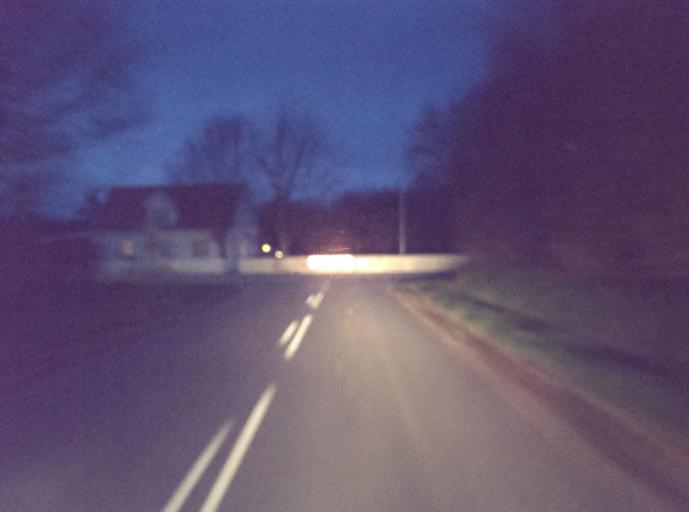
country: DK
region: South Denmark
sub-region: Esbjerg Kommune
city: Esbjerg
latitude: 55.4764
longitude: 8.5092
